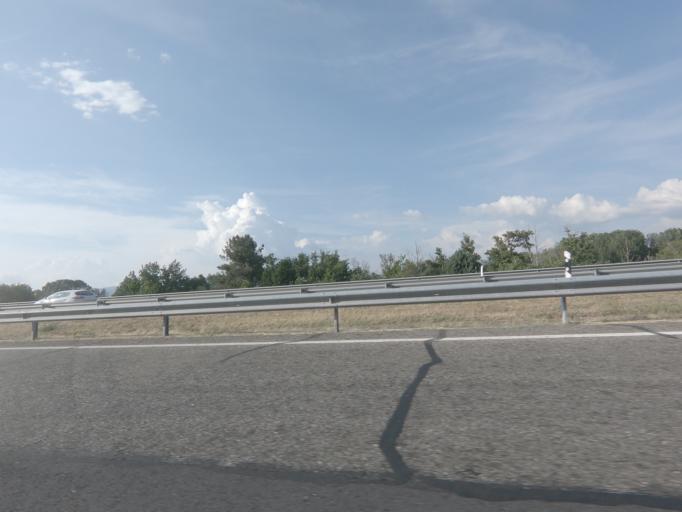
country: ES
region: Galicia
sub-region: Provincia de Ourense
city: Verin
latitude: 41.9207
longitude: -7.4586
